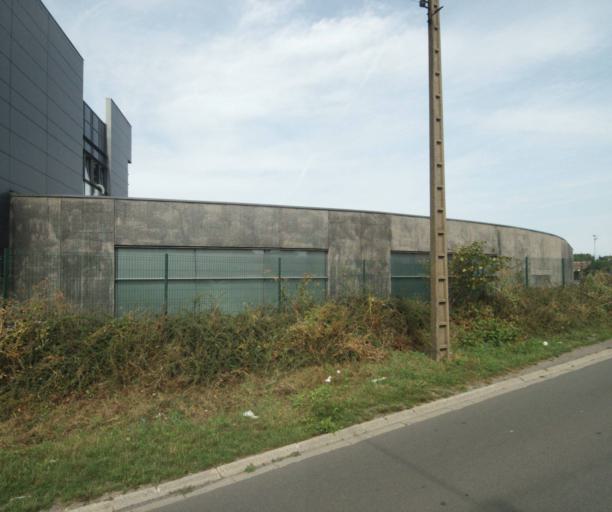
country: FR
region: Nord-Pas-de-Calais
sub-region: Departement du Nord
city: Wattignies
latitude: 50.6004
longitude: 3.0473
